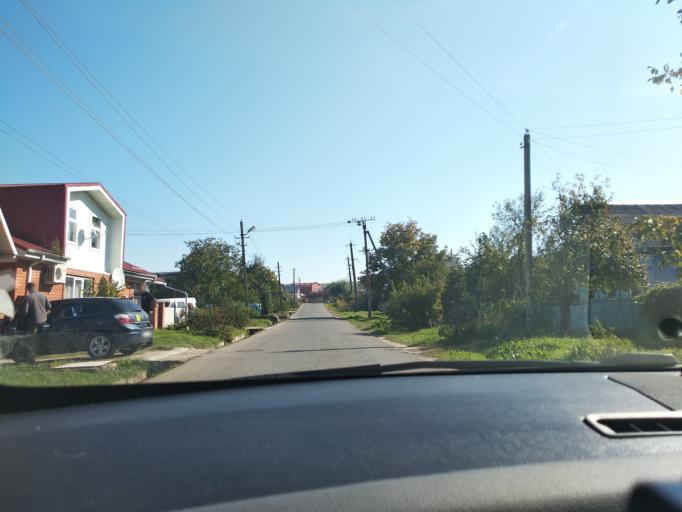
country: RU
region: Krasnodarskiy
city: Goryachiy Klyuch
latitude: 44.6320
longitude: 39.1508
